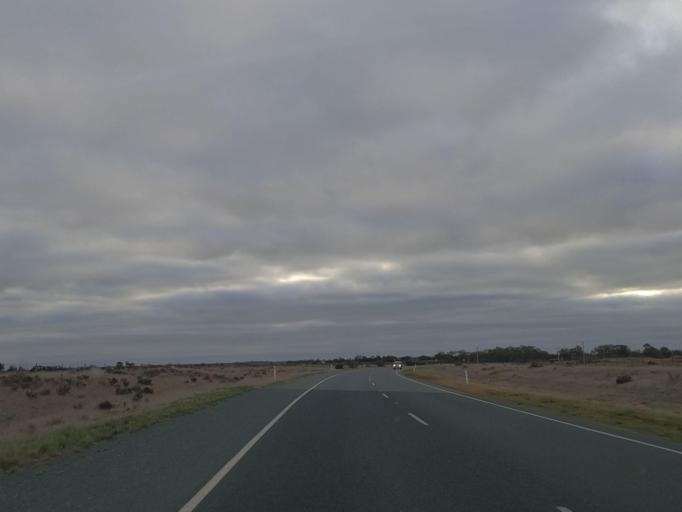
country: AU
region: Victoria
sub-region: Swan Hill
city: Swan Hill
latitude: -35.6255
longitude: 143.8071
